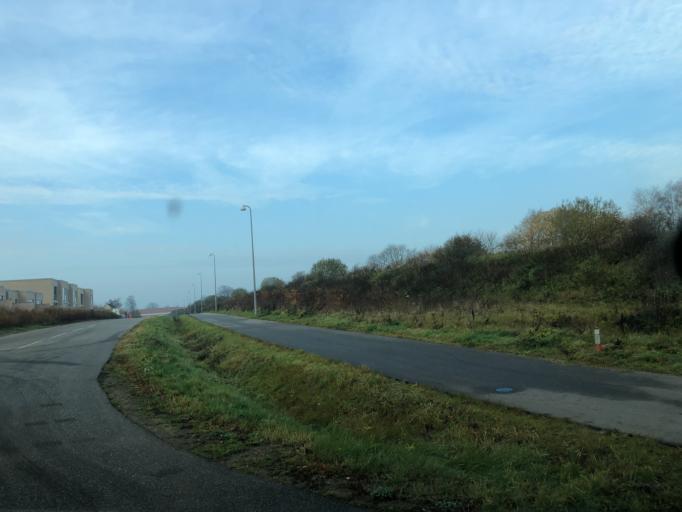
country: DK
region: Central Jutland
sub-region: Silkeborg Kommune
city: Silkeborg
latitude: 56.1480
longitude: 9.4776
